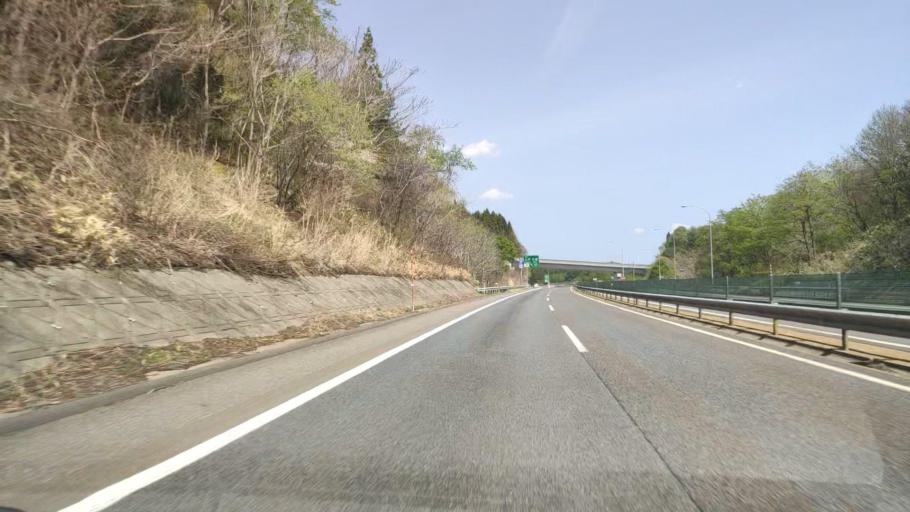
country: JP
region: Iwate
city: Ichinohe
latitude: 40.2482
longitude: 141.4012
